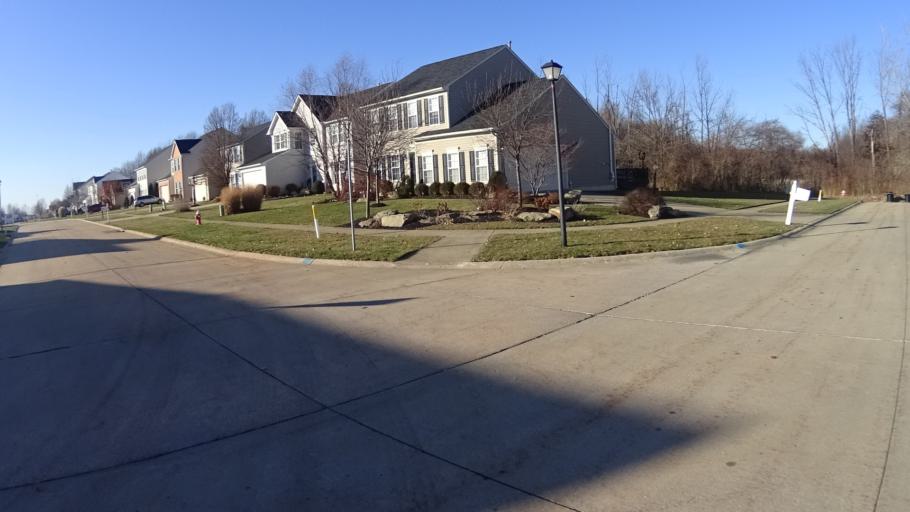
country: US
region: Ohio
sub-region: Lorain County
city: North Ridgeville
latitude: 41.4103
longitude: -82.0442
